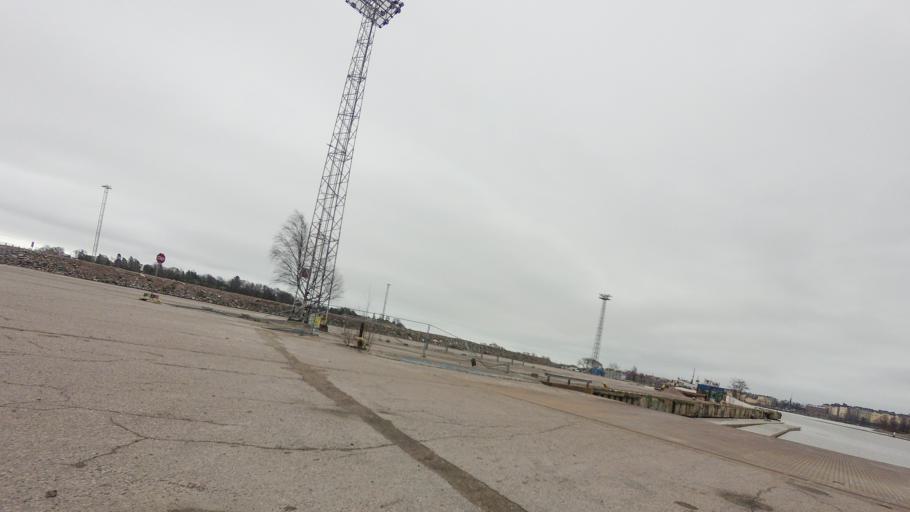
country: FI
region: Uusimaa
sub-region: Helsinki
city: Helsinki
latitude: 60.1773
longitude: 24.9727
